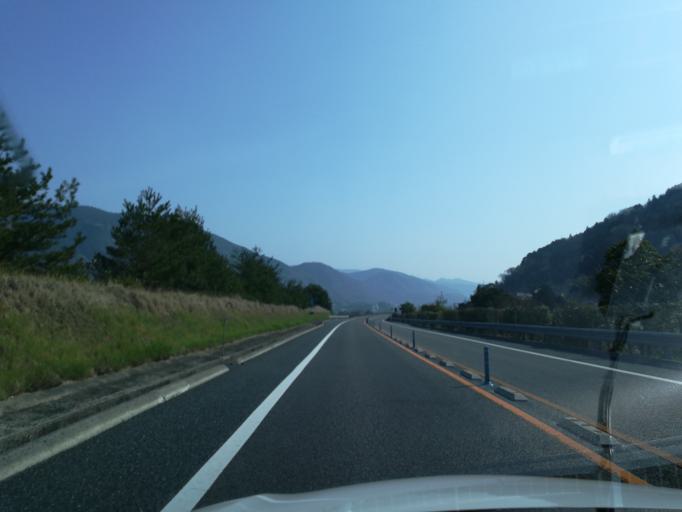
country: JP
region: Tokushima
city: Ikedacho
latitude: 34.0268
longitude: 133.8267
